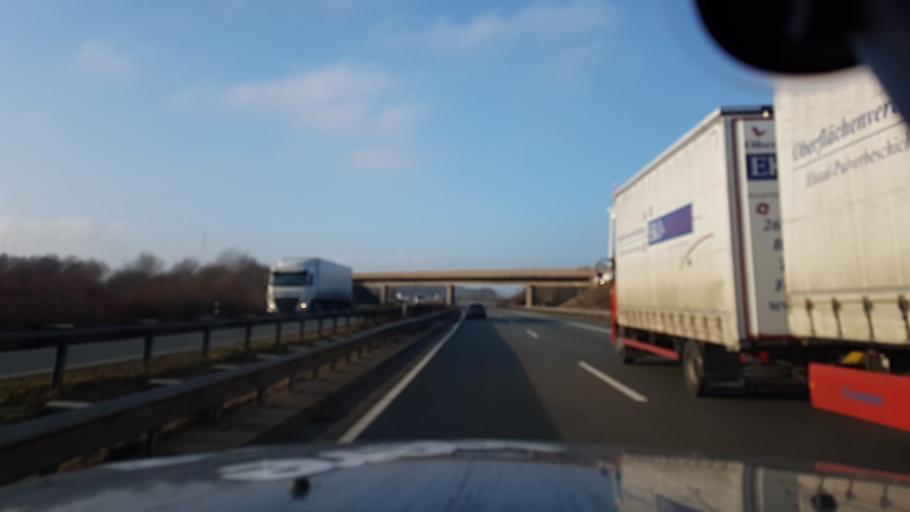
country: DE
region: Lower Saxony
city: Salzbergen
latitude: 52.3405
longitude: 7.4032
